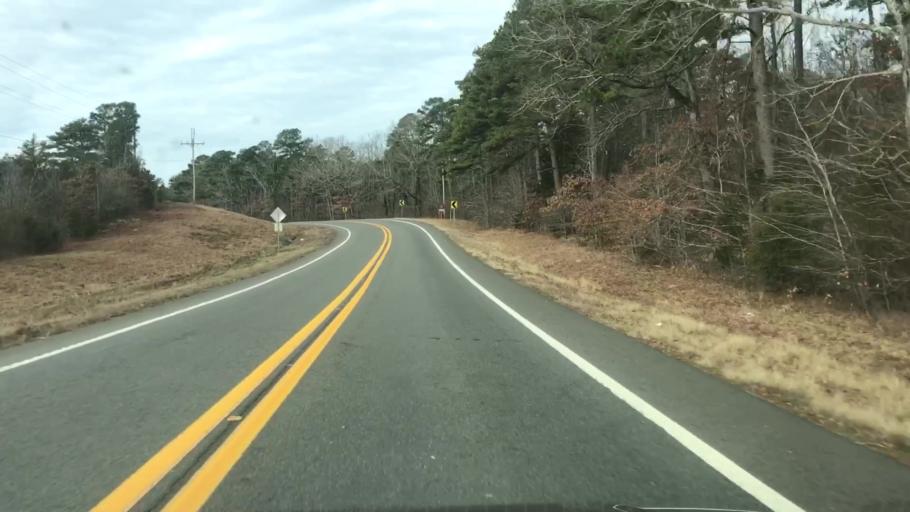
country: US
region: Arkansas
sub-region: Montgomery County
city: Mount Ida
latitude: 34.6199
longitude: -93.7085
